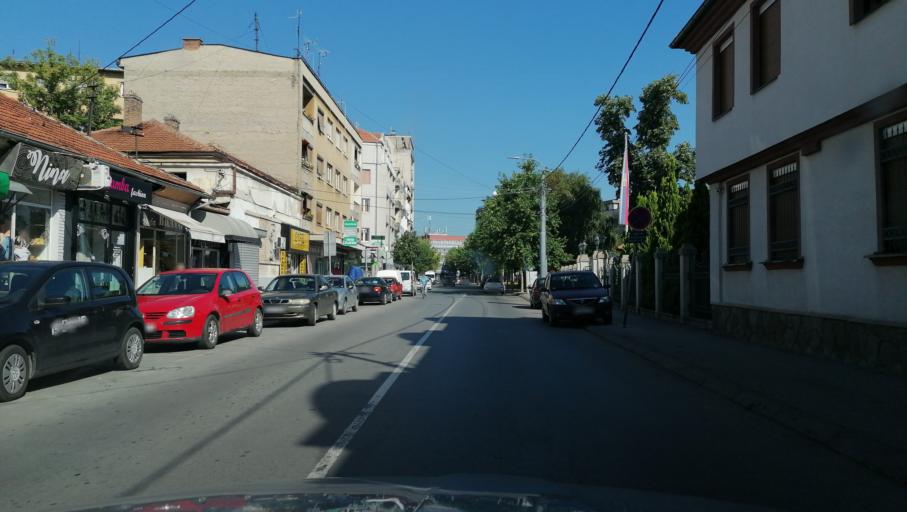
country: RS
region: Central Serbia
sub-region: Rasinski Okrug
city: Krusevac
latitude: 43.5787
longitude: 21.3316
